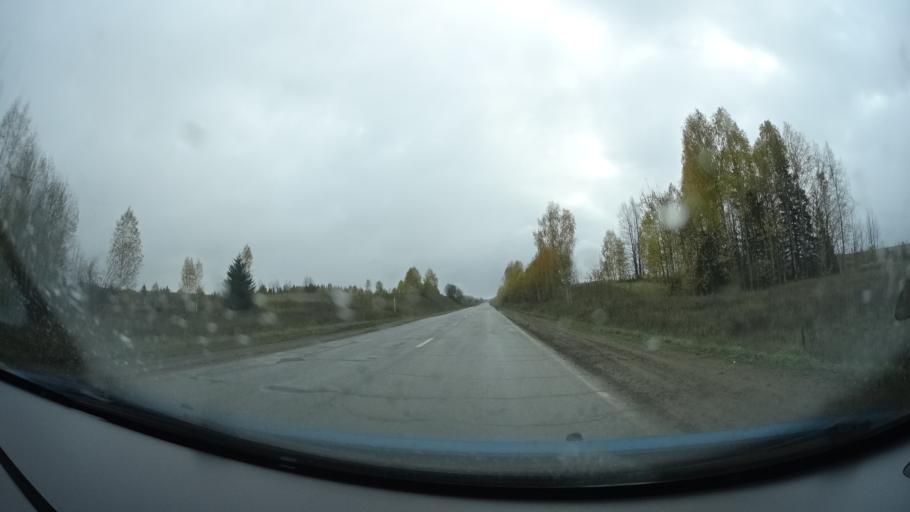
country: RU
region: Perm
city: Chernushka
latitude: 56.7513
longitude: 56.1516
